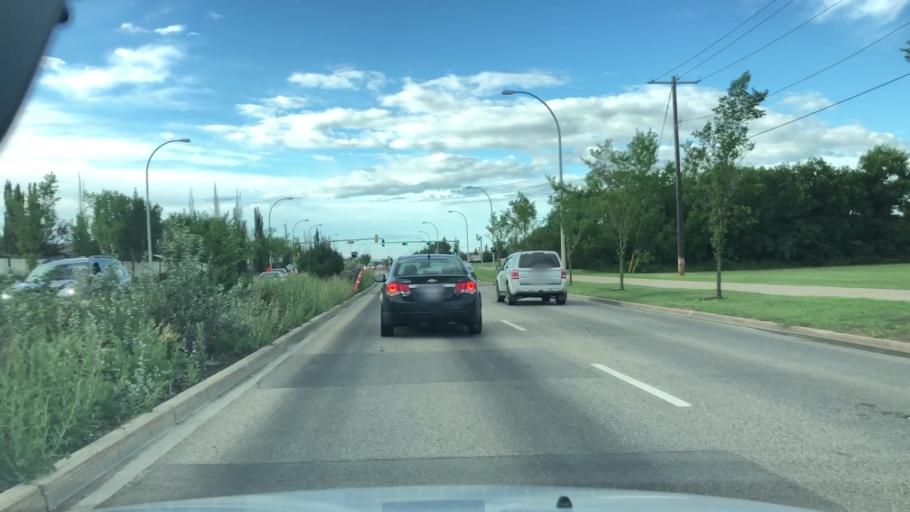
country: CA
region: Alberta
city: St. Albert
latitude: 53.6221
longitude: -113.5411
